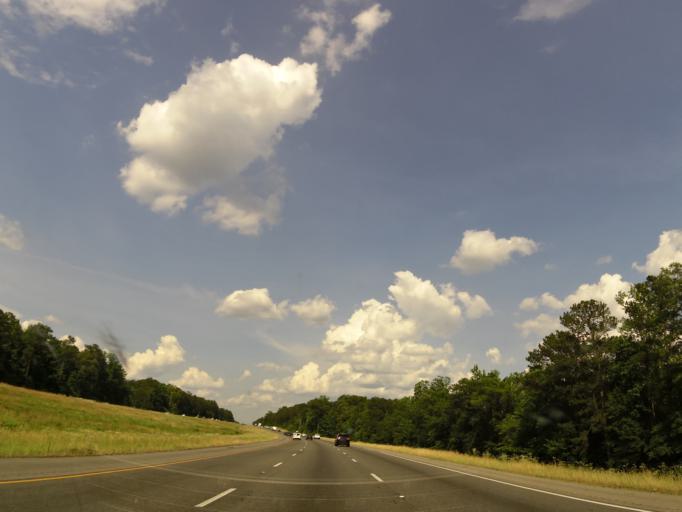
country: US
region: Alabama
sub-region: Tuscaloosa County
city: Coaling
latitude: 33.1838
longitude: -87.3426
